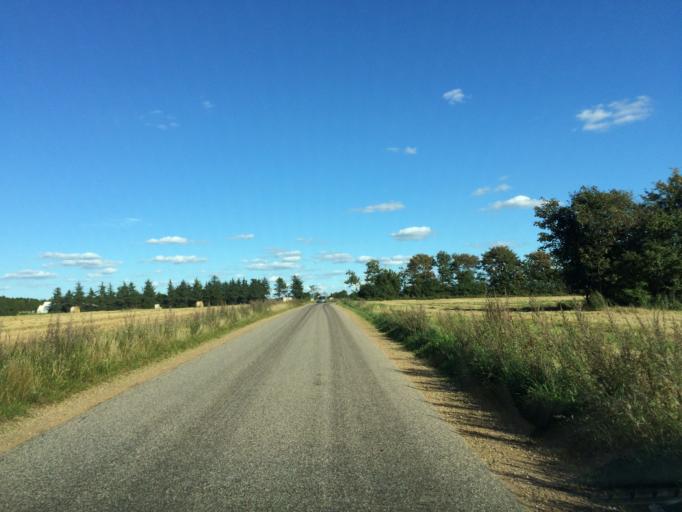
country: DK
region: Central Jutland
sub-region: Holstebro Kommune
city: Holstebro
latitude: 56.3152
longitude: 8.6152
